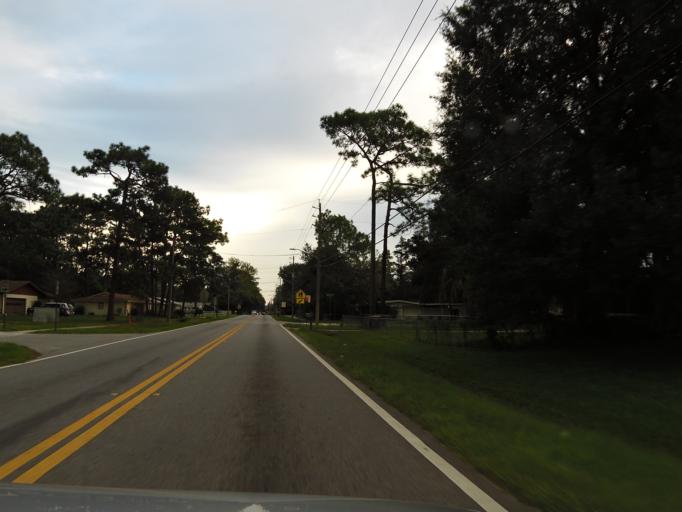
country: US
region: Florida
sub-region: Clay County
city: Bellair-Meadowbrook Terrace
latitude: 30.2843
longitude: -81.7877
